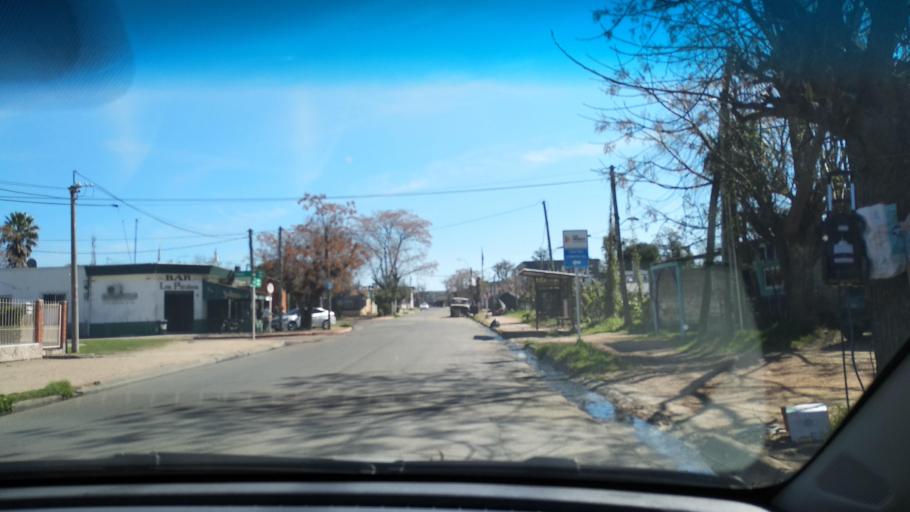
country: UY
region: Canelones
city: Las Piedras
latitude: -34.7280
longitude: -56.2088
